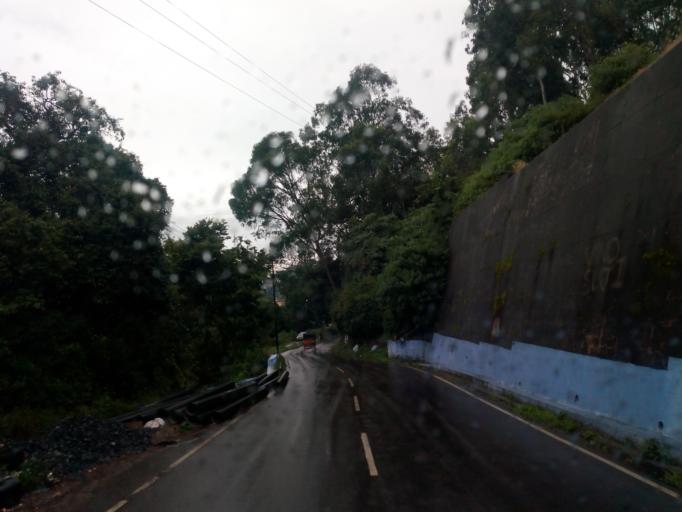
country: IN
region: Tamil Nadu
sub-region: Nilgiri
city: Wellington
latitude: 11.3431
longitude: 76.7984
